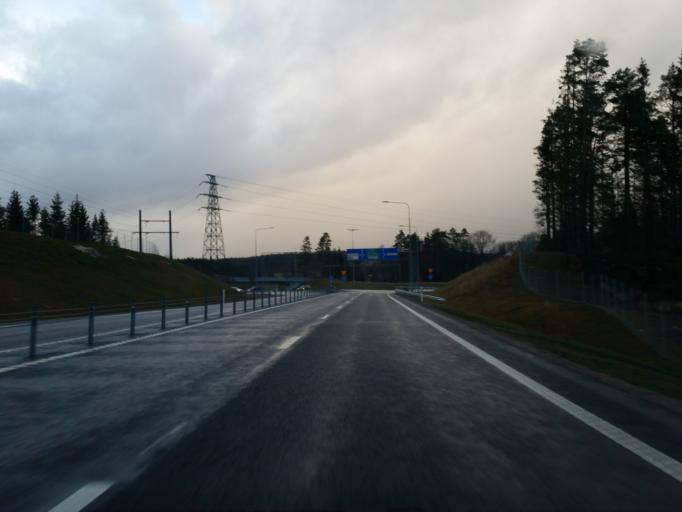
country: SE
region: Vaestra Goetaland
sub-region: Boras Kommun
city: Sjomarken
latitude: 57.7069
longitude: 12.8725
